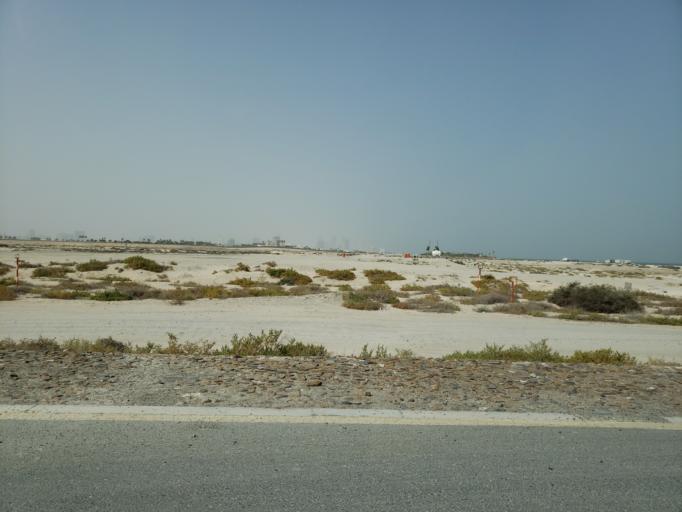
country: AE
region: Ajman
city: Ajman
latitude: 25.4464
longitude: 55.4724
